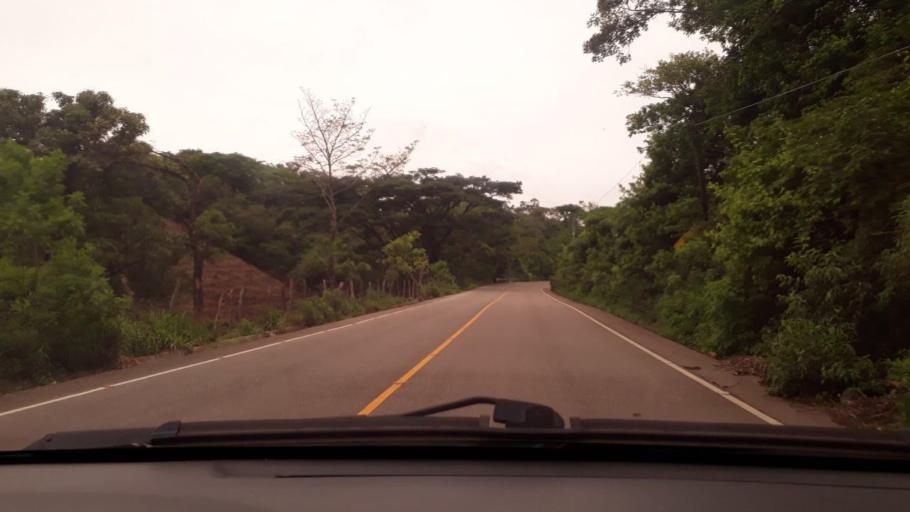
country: GT
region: Chiquimula
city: Concepcion Las Minas
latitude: 14.4590
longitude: -89.4646
